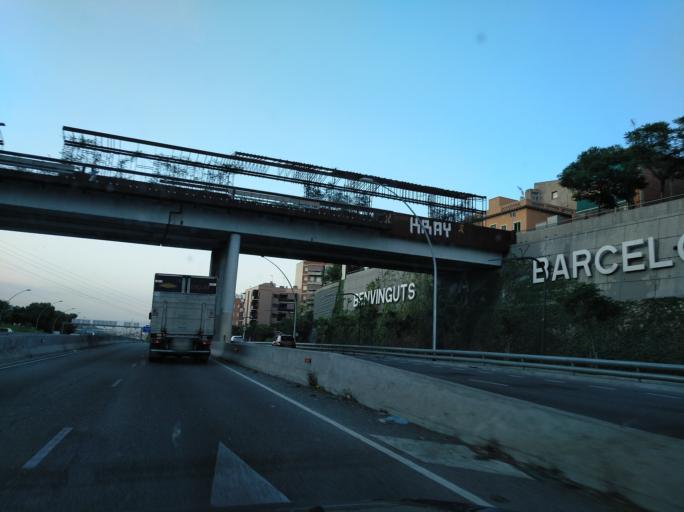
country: ES
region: Catalonia
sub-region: Provincia de Barcelona
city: Nou Barris
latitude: 41.4511
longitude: 2.1890
